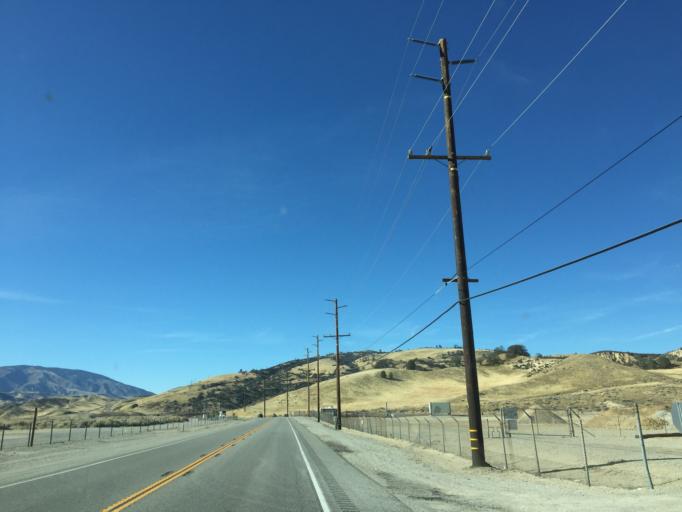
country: US
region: California
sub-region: Kern County
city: Lebec
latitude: 34.7718
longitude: -118.7594
